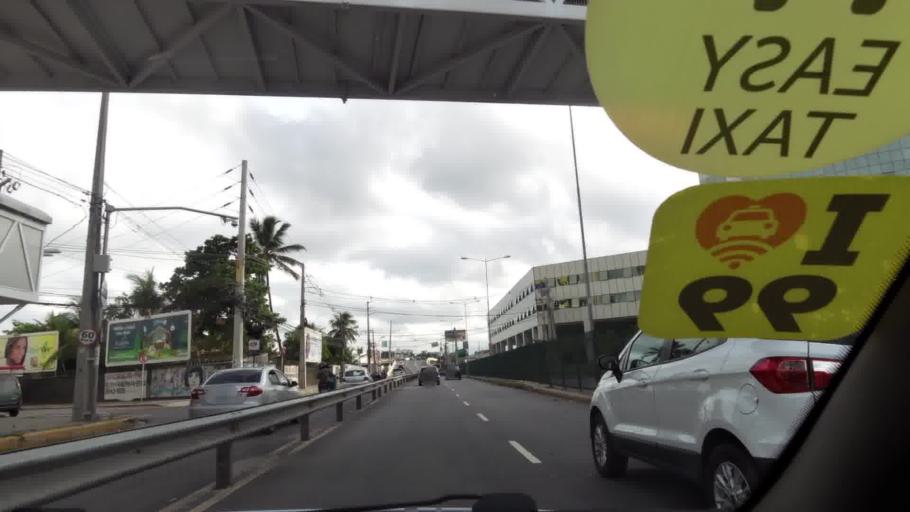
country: BR
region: Pernambuco
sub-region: Recife
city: Recife
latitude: -8.0866
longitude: -34.8913
